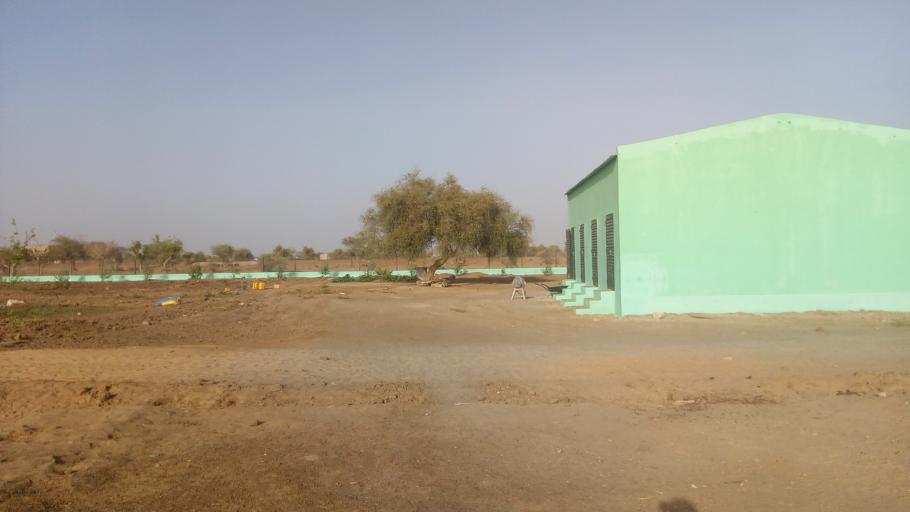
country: ML
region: Kayes
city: Nioro
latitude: 15.0357
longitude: -9.3664
